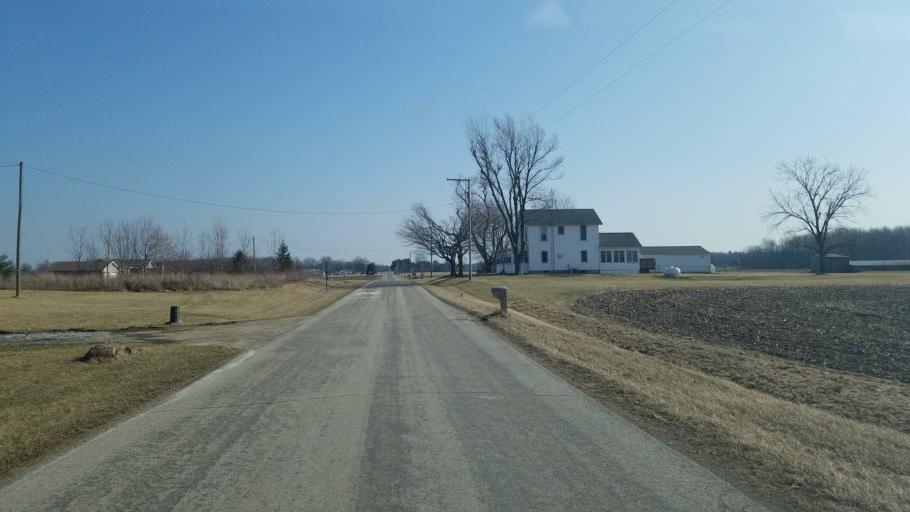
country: US
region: Ohio
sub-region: Crawford County
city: Crestline
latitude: 40.8142
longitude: -82.7134
